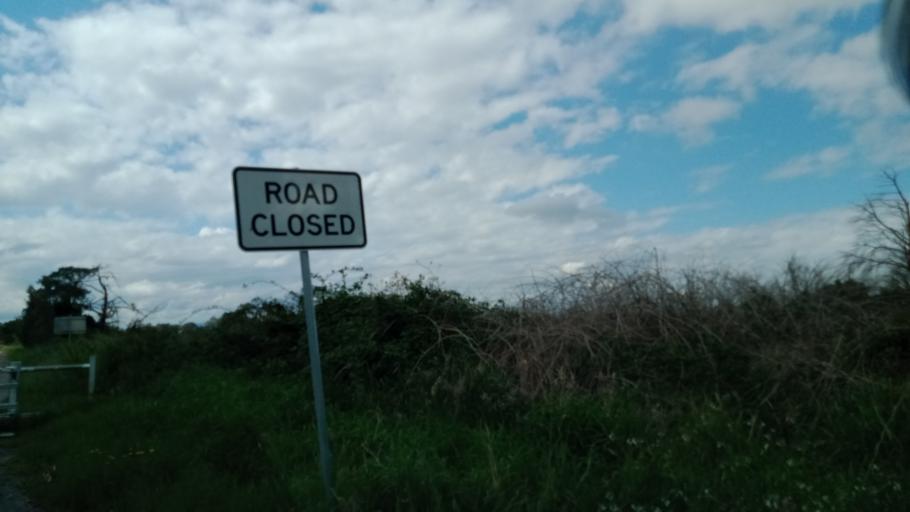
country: AU
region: Victoria
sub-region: Frankston
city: Sandhurst
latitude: -38.0822
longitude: 145.2201
